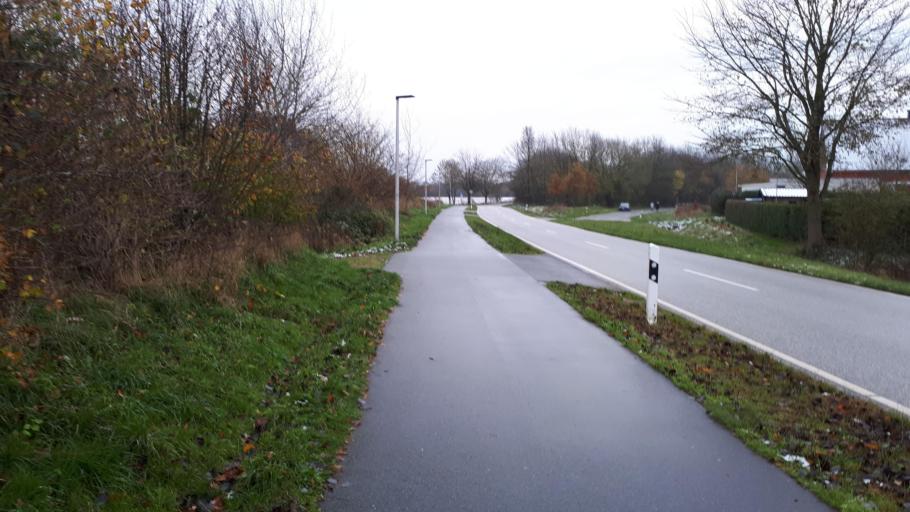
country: DE
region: Schleswig-Holstein
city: Tastrup
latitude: 54.7724
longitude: 9.4735
